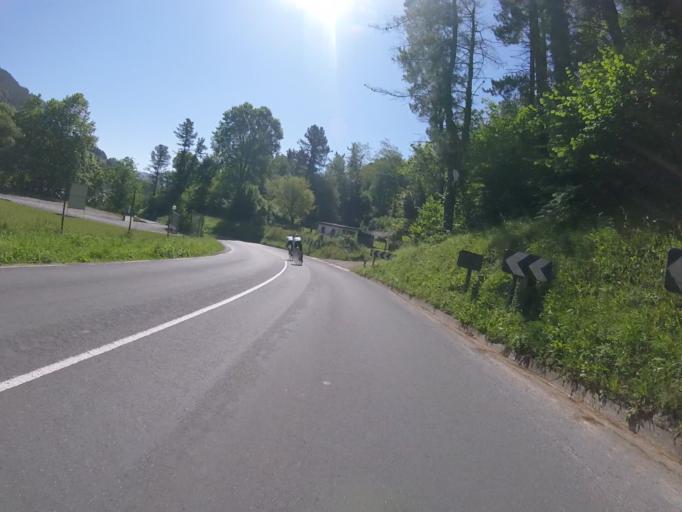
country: ES
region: Basque Country
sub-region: Provincia de Guipuzcoa
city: Albiztur
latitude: 43.1243
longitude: -2.1181
